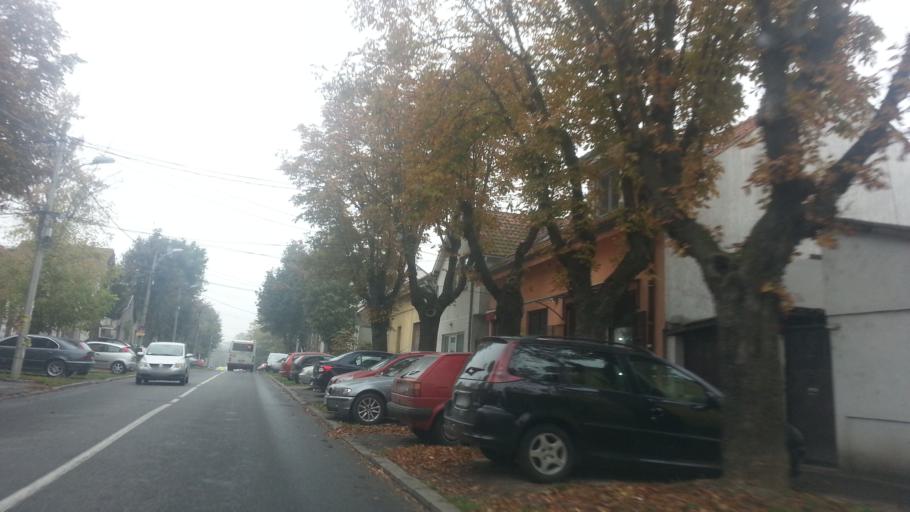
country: RS
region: Central Serbia
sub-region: Belgrade
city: Zemun
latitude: 44.8401
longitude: 20.3840
